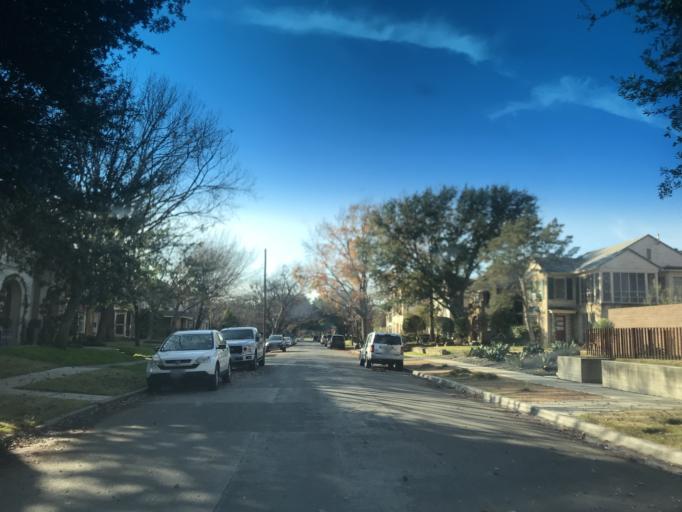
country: US
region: Texas
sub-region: Dallas County
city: Highland Park
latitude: 32.8207
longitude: -96.8054
